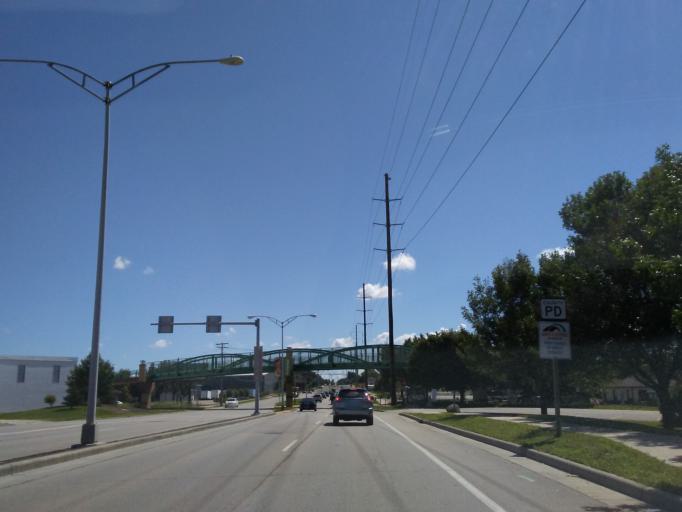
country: US
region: Wisconsin
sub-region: Dane County
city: Fitchburg
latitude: 43.0154
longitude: -89.4716
